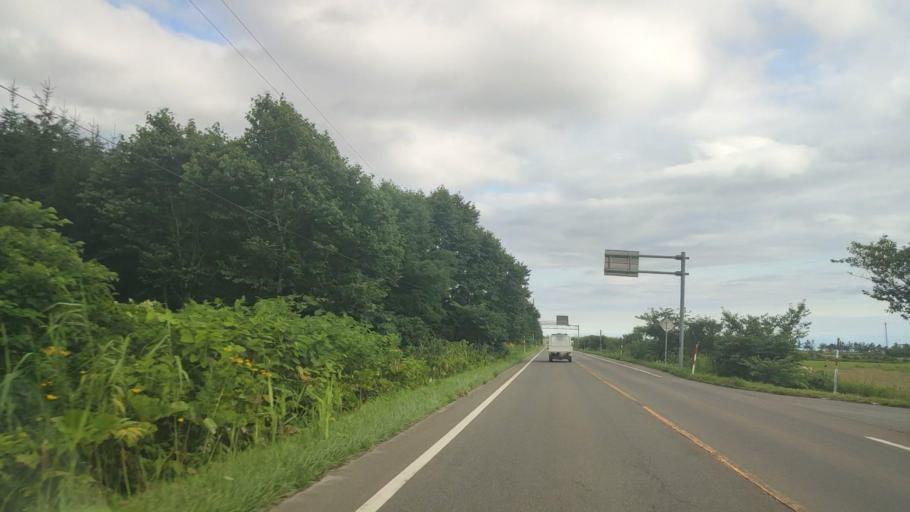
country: JP
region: Hokkaido
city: Niseko Town
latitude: 42.5857
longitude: 140.4503
